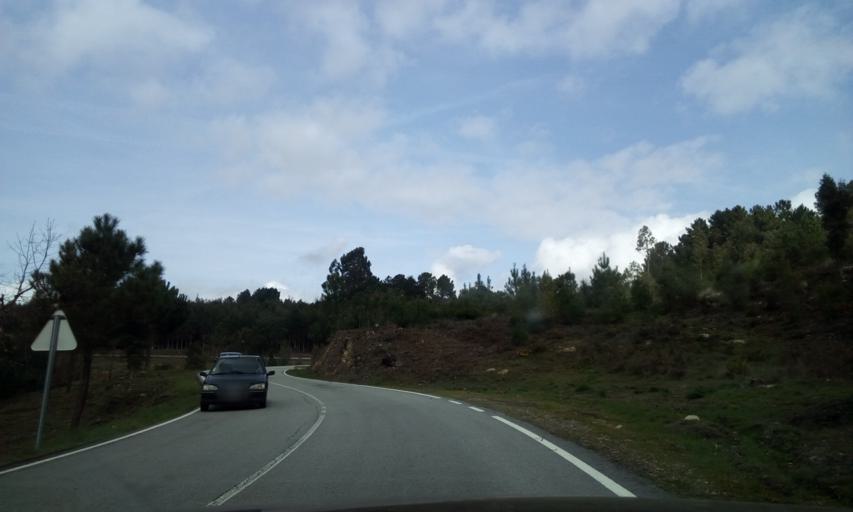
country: PT
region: Viseu
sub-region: Satao
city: Satao
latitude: 40.6667
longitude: -7.6840
